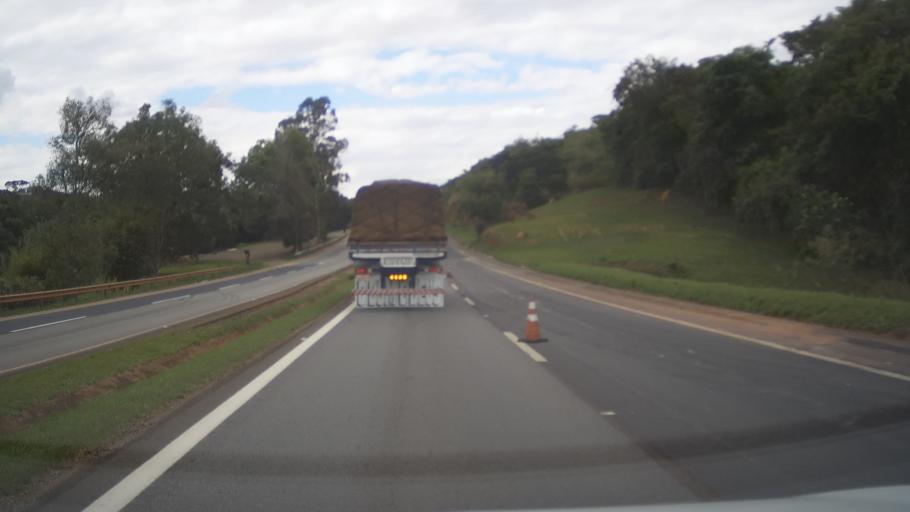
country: BR
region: Minas Gerais
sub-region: Itauna
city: Itauna
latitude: -20.3202
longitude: -44.4556
